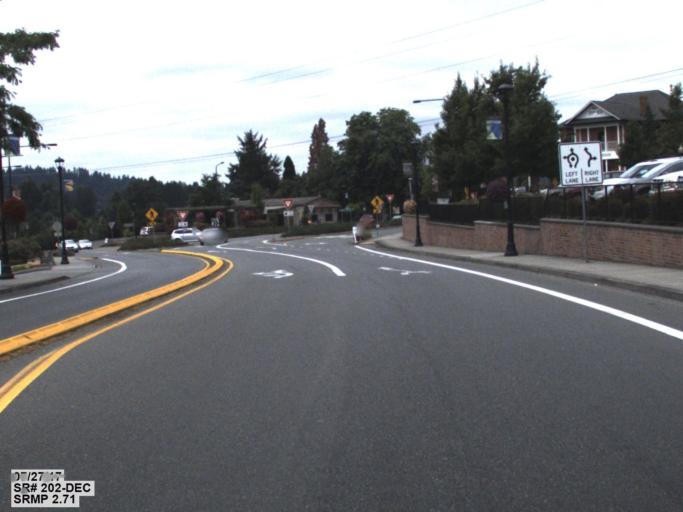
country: US
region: Washington
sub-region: King County
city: Woodinville
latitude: 47.7324
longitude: -122.1417
